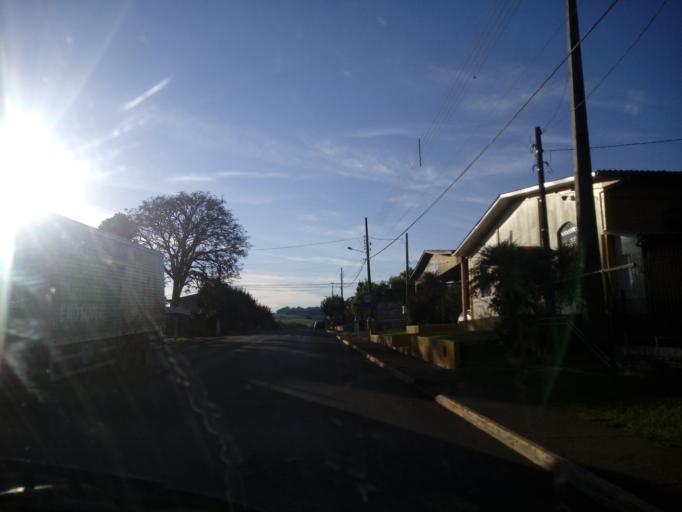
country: BR
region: Santa Catarina
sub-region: Chapeco
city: Chapeco
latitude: -27.0351
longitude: -52.6318
